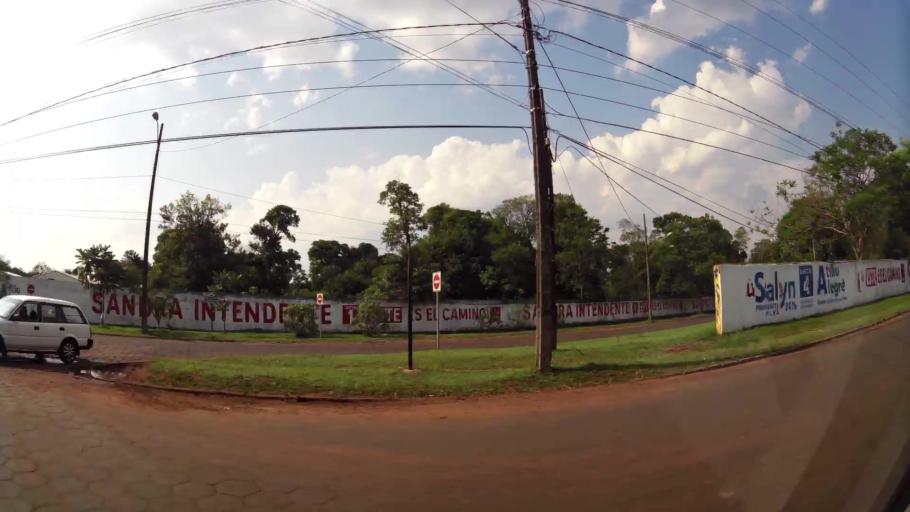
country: PY
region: Alto Parana
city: Presidente Franco
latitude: -25.5252
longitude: -54.6169
